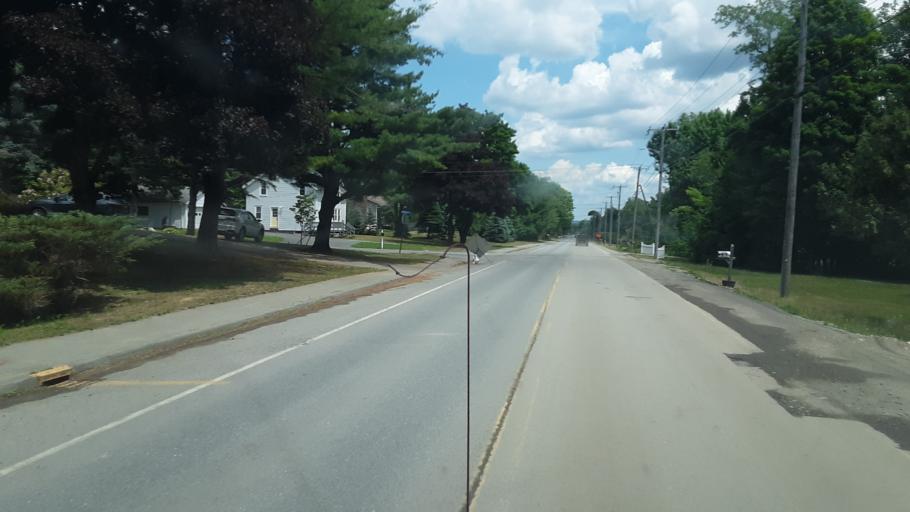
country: US
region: Maine
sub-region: Penobscot County
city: Hampden
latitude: 44.7612
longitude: -68.8099
